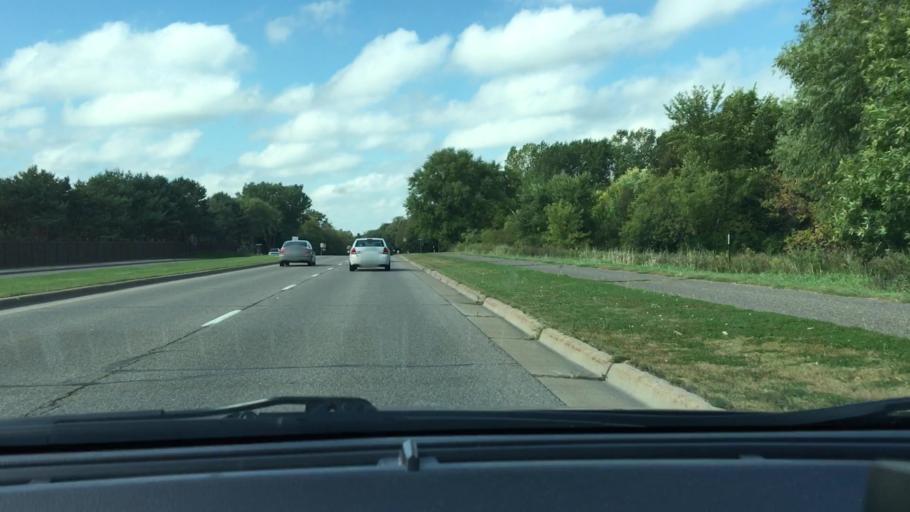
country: US
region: Minnesota
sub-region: Hennepin County
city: Maple Grove
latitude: 45.0585
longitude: -93.4233
